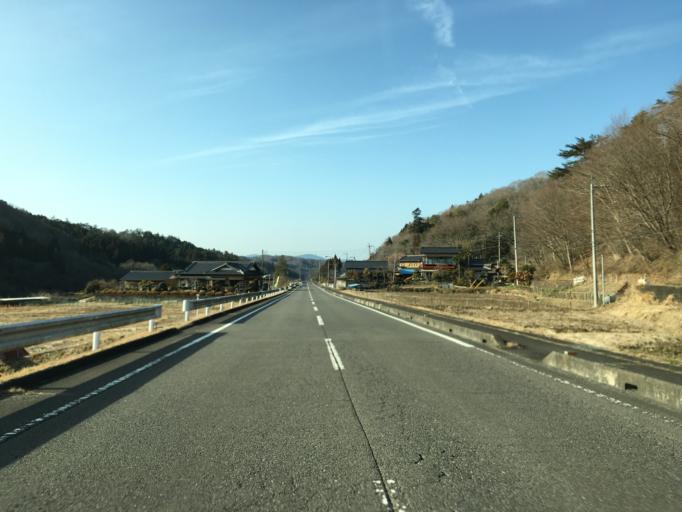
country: JP
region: Ibaraki
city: Daigo
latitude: 36.7522
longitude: 140.4412
